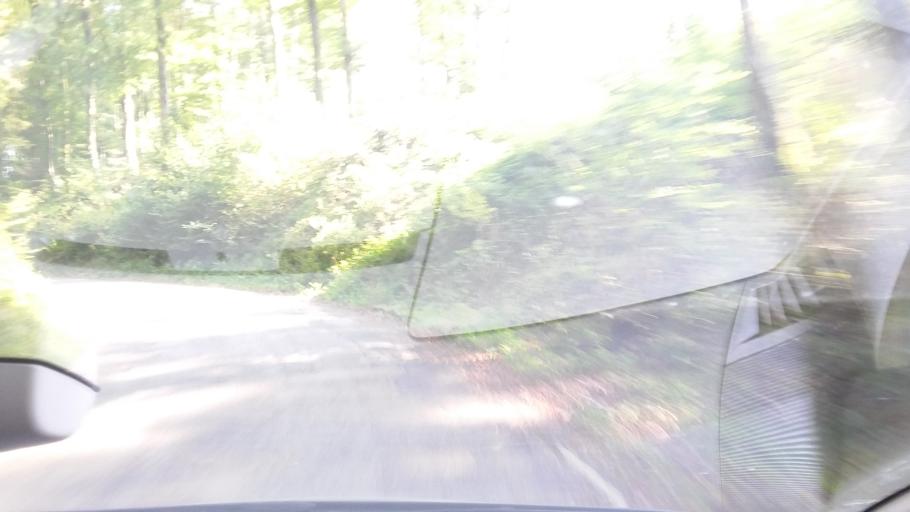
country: LU
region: Luxembourg
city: Eischen
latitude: 49.7061
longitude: 5.8635
